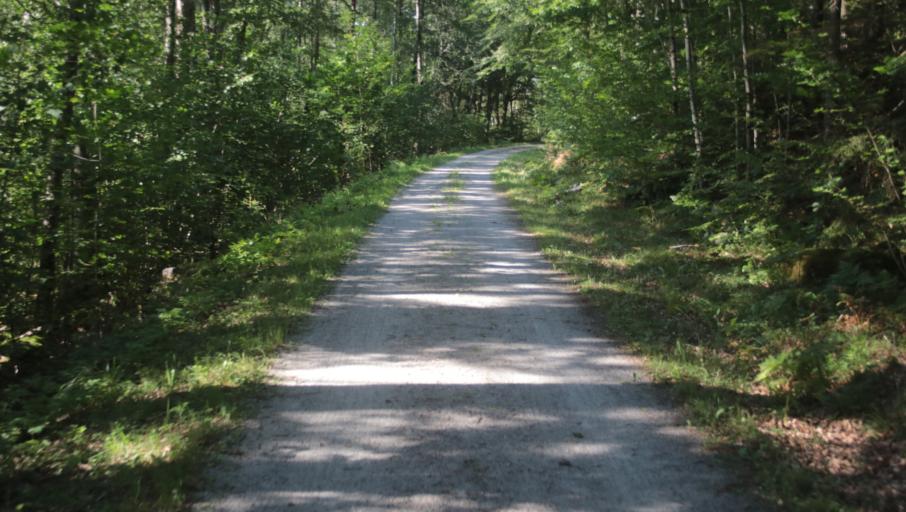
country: SE
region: Blekinge
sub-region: Karlshamns Kommun
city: Svangsta
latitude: 56.3739
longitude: 14.6817
